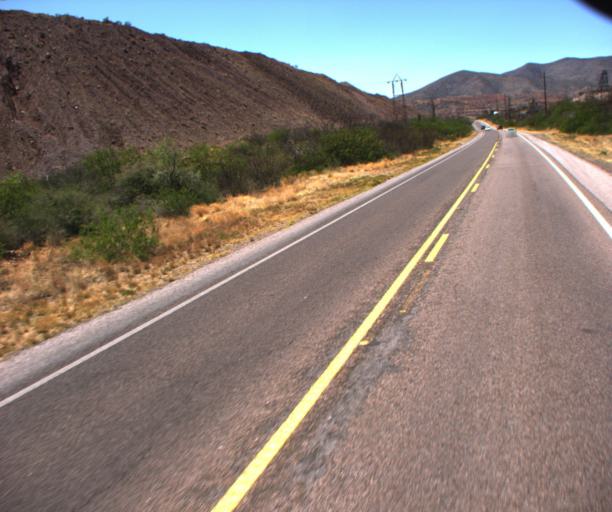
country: US
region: Arizona
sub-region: Cochise County
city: Bisbee
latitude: 31.4297
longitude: -109.8714
